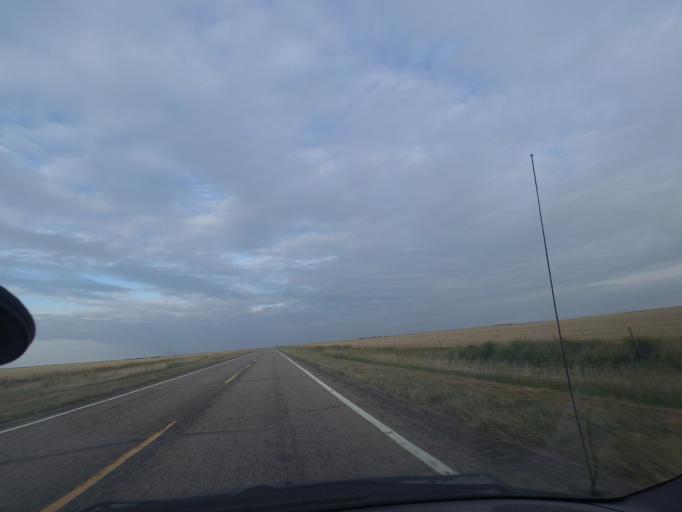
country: US
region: Colorado
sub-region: Yuma County
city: Wray
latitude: 39.7462
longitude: -102.2360
